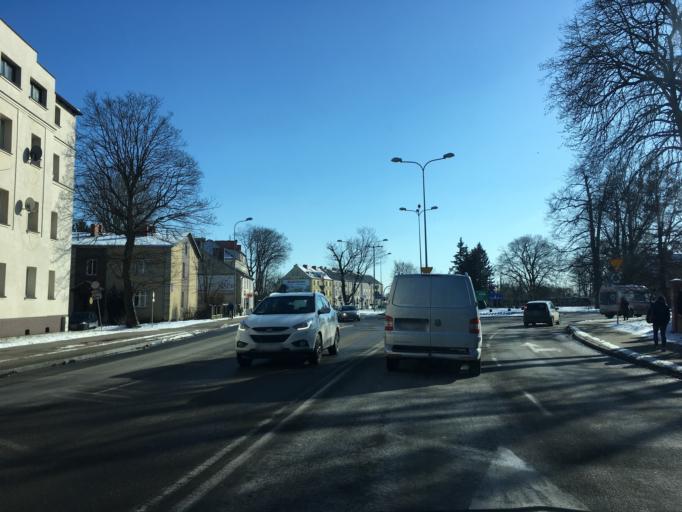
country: PL
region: Pomeranian Voivodeship
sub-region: Slupsk
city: Slupsk
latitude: 54.4644
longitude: 17.0113
